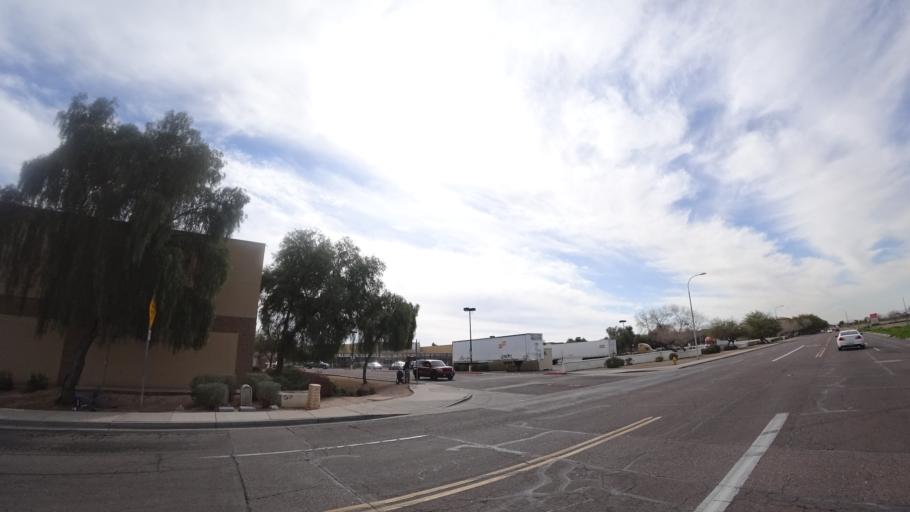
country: US
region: Arizona
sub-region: Maricopa County
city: Tolleson
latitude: 33.4729
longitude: -112.2226
